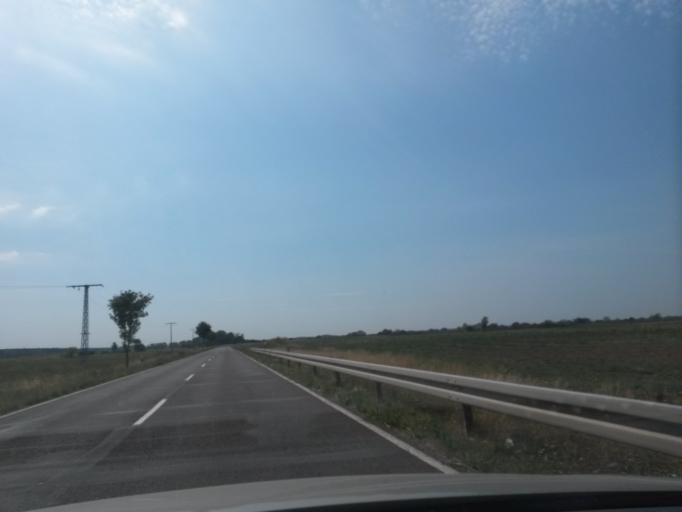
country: DE
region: Saxony-Anhalt
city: Jerichow
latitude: 52.4660
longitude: 12.0157
